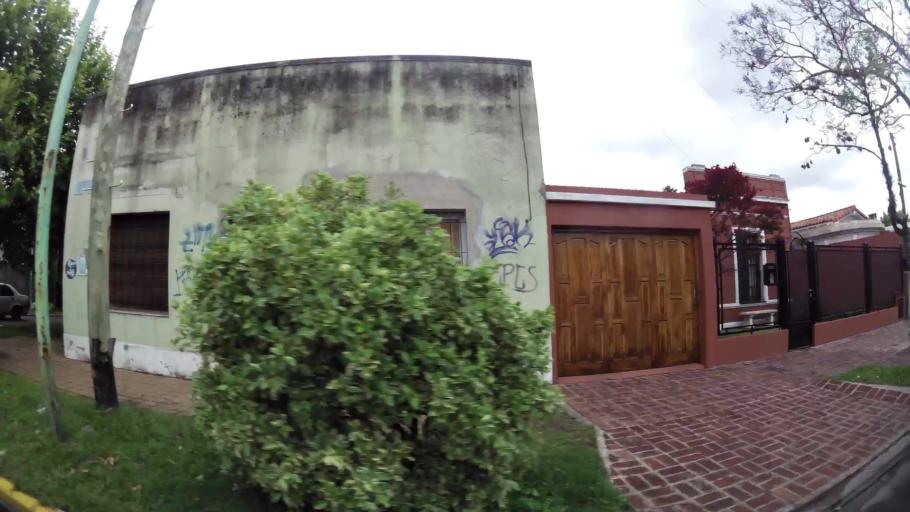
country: AR
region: Buenos Aires
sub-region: Partido de Lomas de Zamora
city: Lomas de Zamora
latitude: -34.7636
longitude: -58.3908
